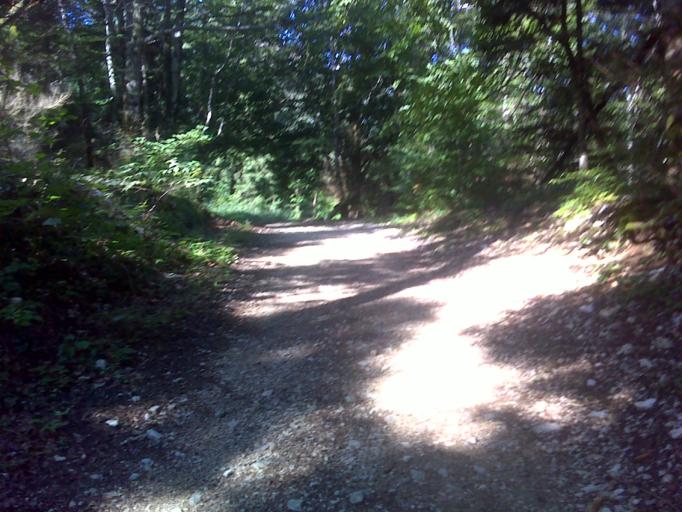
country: FR
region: Rhone-Alpes
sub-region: Departement de l'Ain
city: Nantua
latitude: 46.1618
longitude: 5.6181
